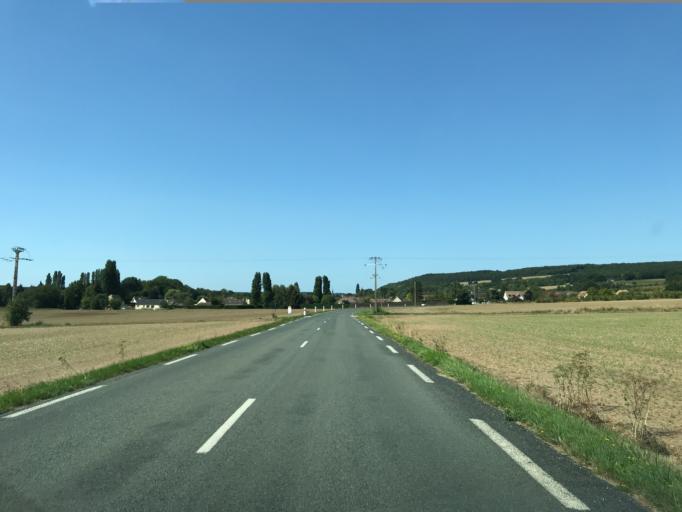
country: FR
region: Haute-Normandie
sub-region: Departement de l'Eure
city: Heudreville-sur-Eure
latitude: 49.1214
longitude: 1.2205
